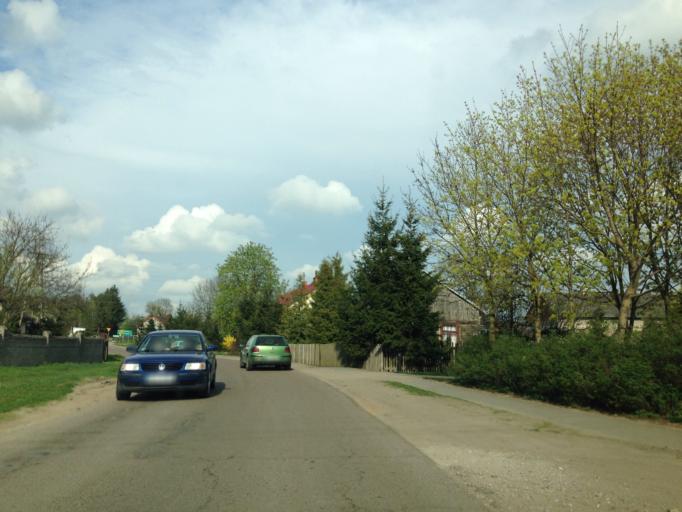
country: PL
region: Masovian Voivodeship
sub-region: Powiat zurominski
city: Zuromin
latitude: 53.0723
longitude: 19.8698
